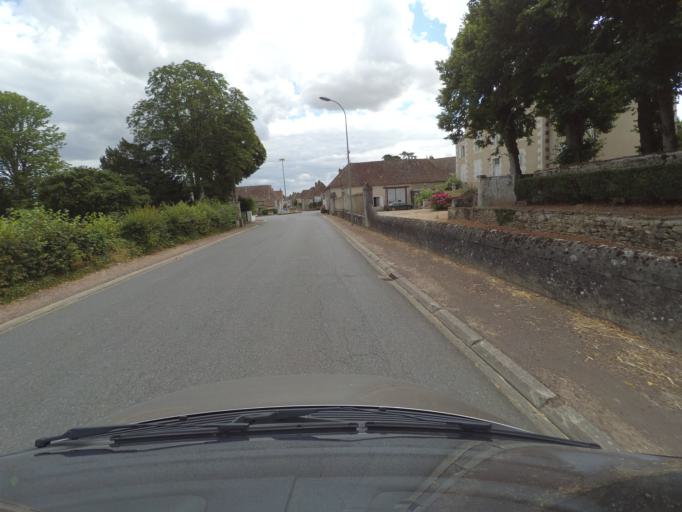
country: FR
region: Centre
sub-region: Departement de l'Indre
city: Belabre
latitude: 46.4689
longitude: 1.0382
